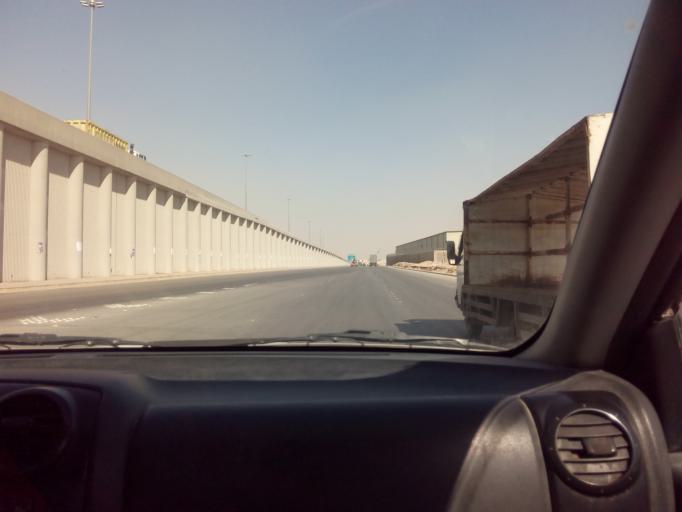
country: SA
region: Ar Riyad
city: Riyadh
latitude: 24.6462
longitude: 46.8417
